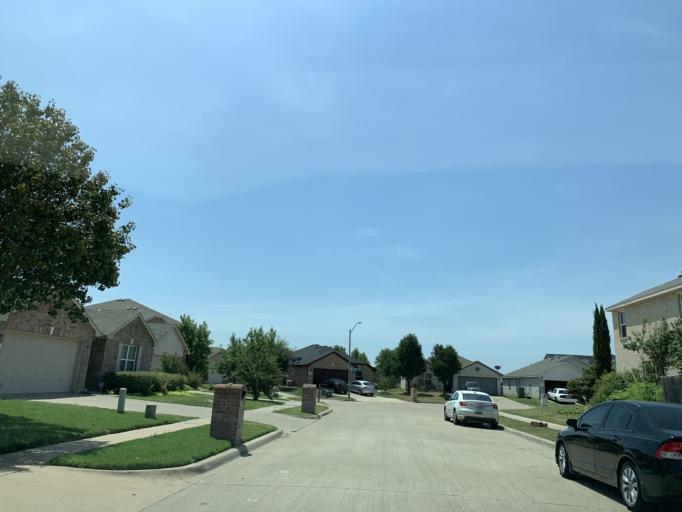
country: US
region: Texas
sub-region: Dallas County
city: Cedar Hill
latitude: 32.6420
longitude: -97.0309
